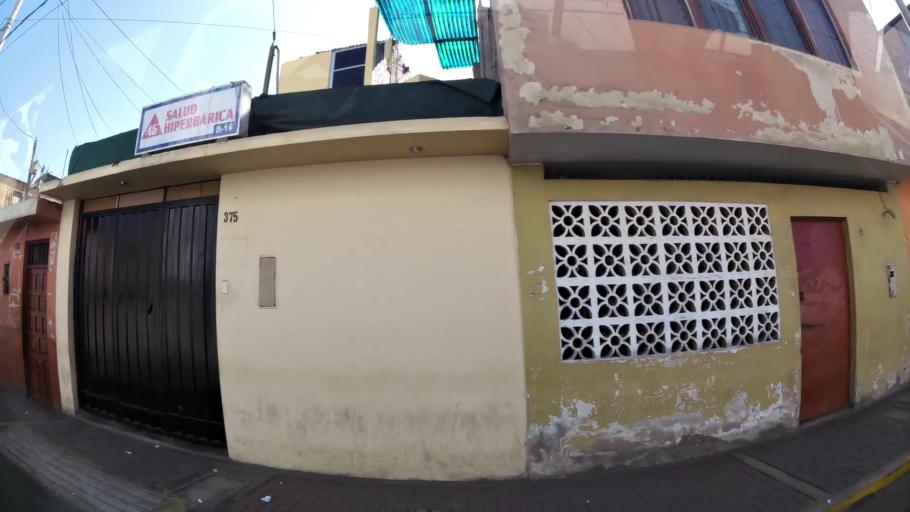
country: PE
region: Ica
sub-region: Provincia de Chincha
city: Chincha Alta
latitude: -13.4158
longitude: -76.1304
